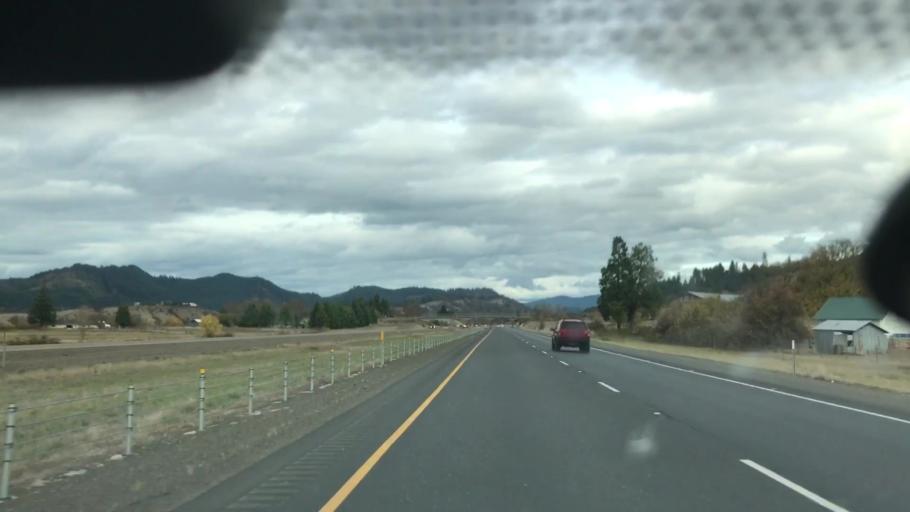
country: US
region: Oregon
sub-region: Douglas County
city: Yoncalla
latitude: 43.5758
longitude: -123.2657
